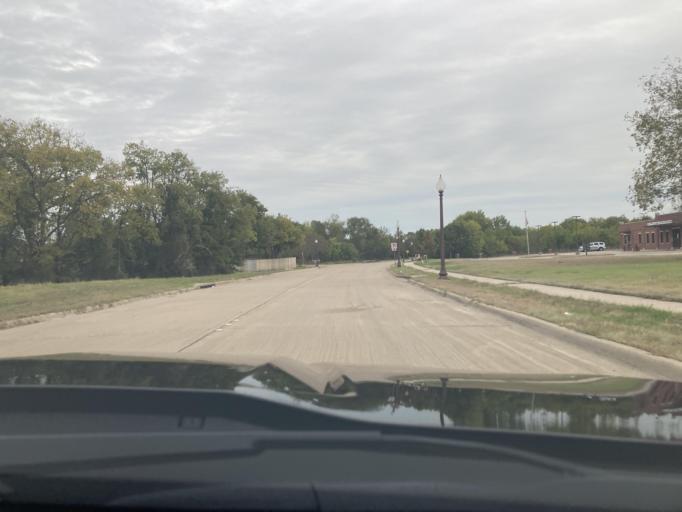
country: US
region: Texas
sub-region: Ellis County
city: Ennis
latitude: 32.3350
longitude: -96.6127
